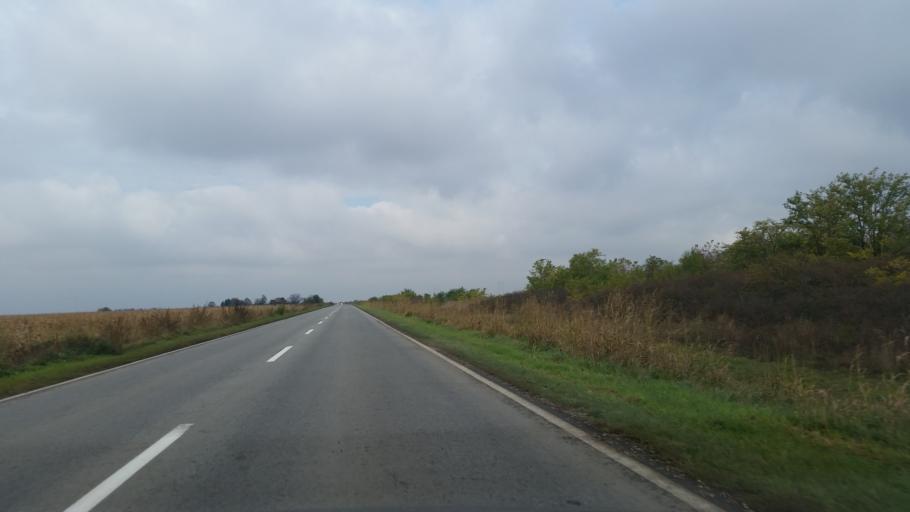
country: RS
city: Mihajlovo
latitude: 45.4410
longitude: 20.3627
